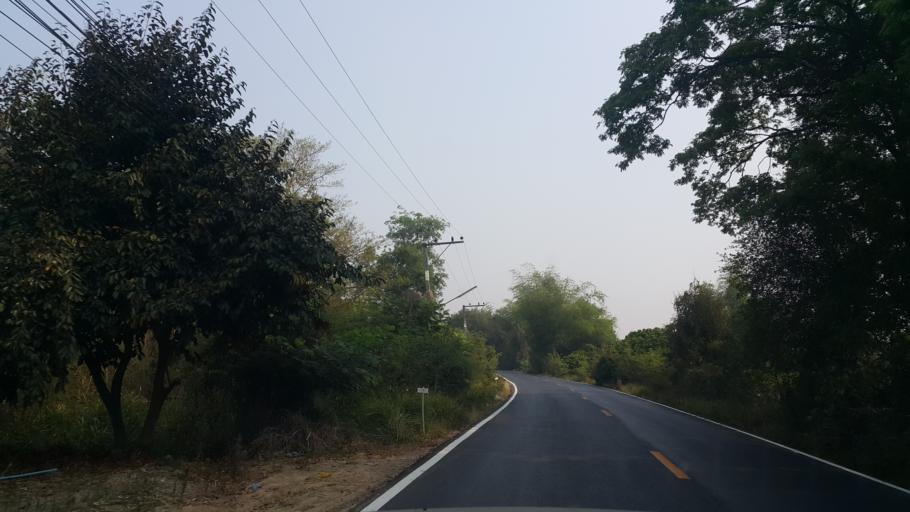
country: TH
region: Chiang Mai
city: Saraphi
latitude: 18.6780
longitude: 99.0757
